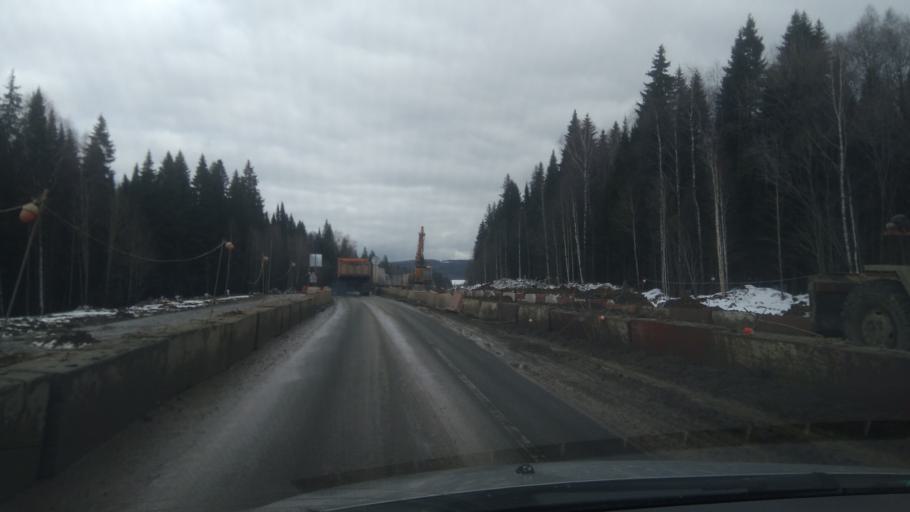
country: RU
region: Sverdlovsk
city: Bisert'
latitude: 56.8296
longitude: 59.1301
